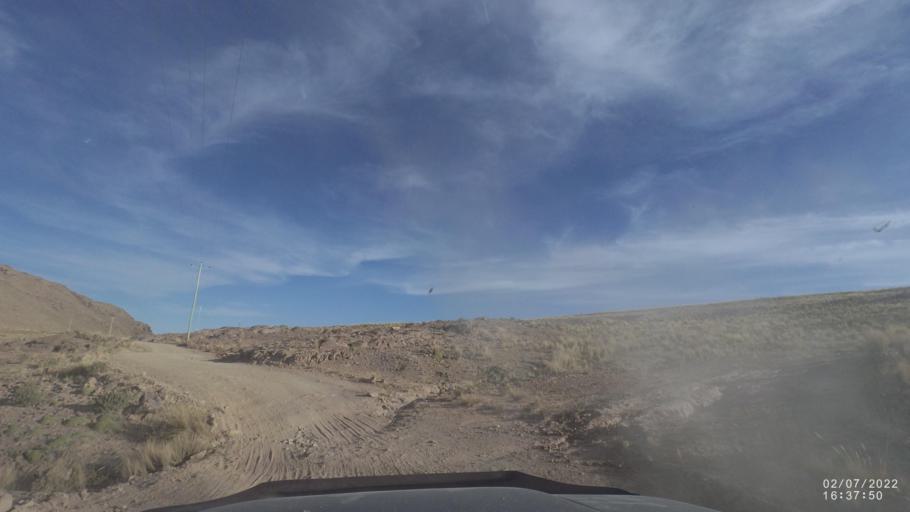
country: BO
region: Cochabamba
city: Irpa Irpa
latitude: -17.9678
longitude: -66.4975
